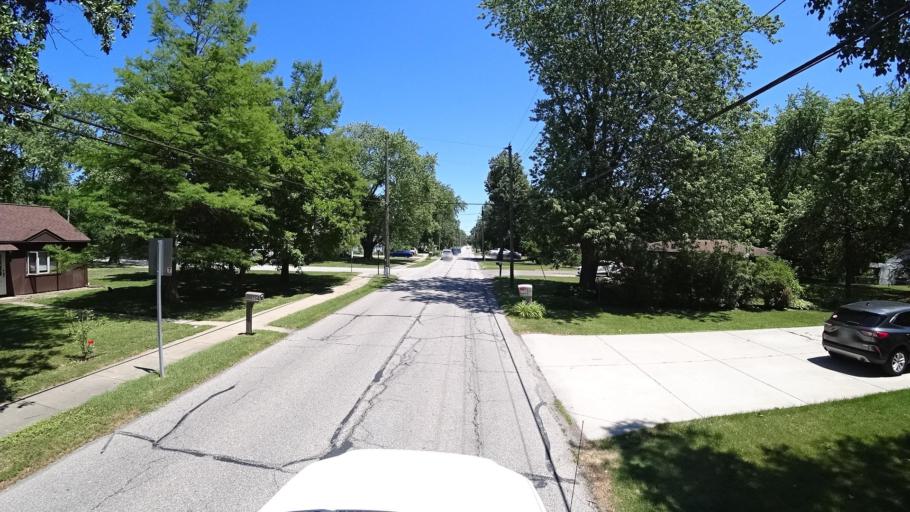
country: US
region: Indiana
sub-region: Porter County
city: Chesterton
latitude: 41.6167
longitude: -87.0627
